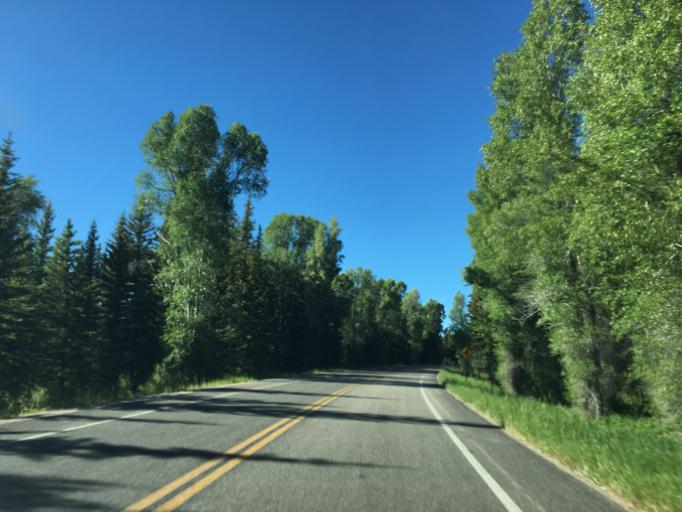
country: US
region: Wyoming
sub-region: Teton County
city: Jackson
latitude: 43.8361
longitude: -110.5134
